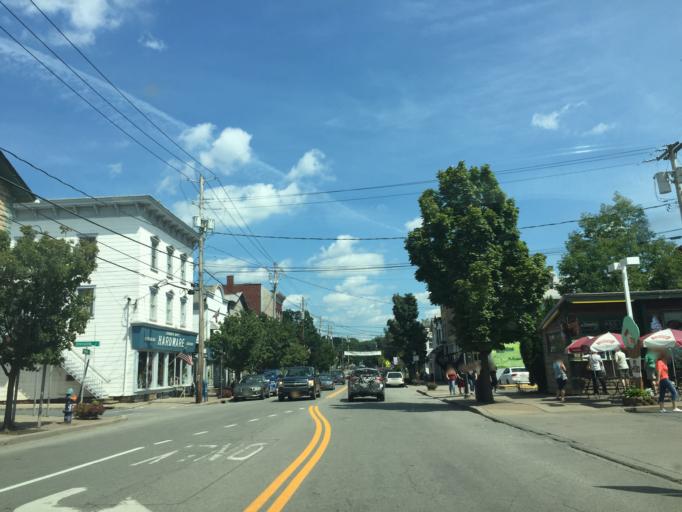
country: US
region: New York
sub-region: Delaware County
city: Delhi
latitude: 42.2764
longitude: -74.9180
